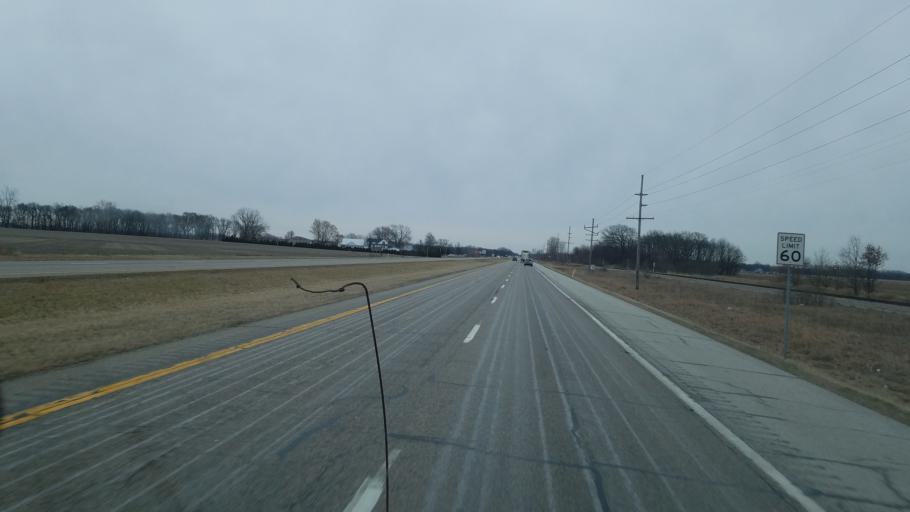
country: US
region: Indiana
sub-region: LaPorte County
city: Kingsford Heights
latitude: 41.4045
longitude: -86.7298
